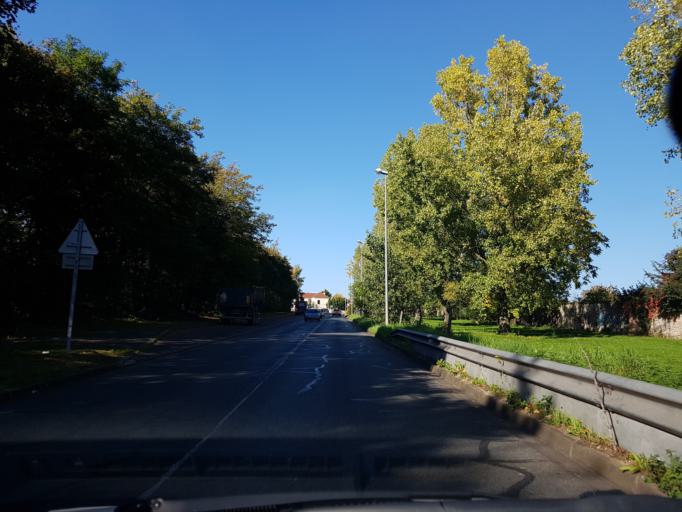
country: FR
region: Ile-de-France
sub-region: Departement du Val-de-Marne
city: Ormesson-sur-Marne
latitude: 48.7827
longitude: 2.5381
